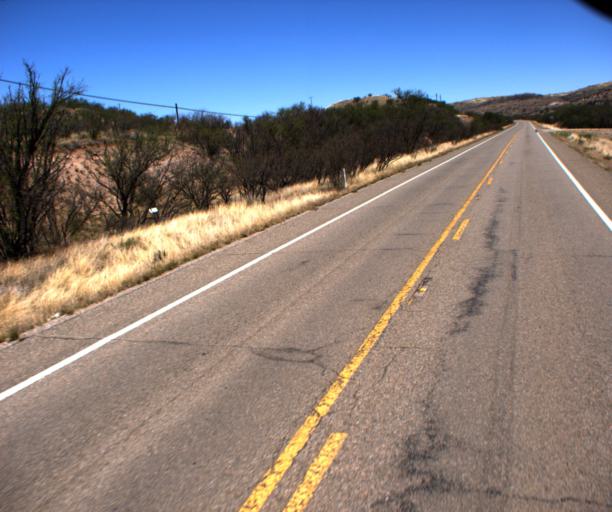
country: US
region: Arizona
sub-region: Santa Cruz County
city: Rio Rico
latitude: 31.6220
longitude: -110.7181
